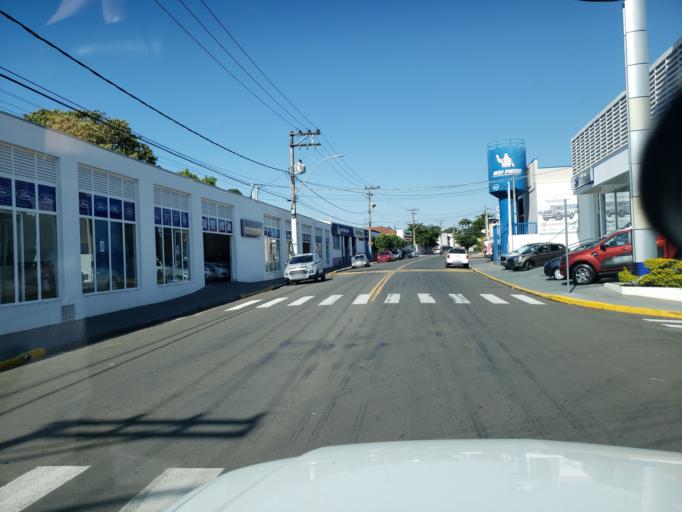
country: BR
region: Sao Paulo
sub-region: Itapira
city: Itapira
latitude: -22.4403
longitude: -46.8317
